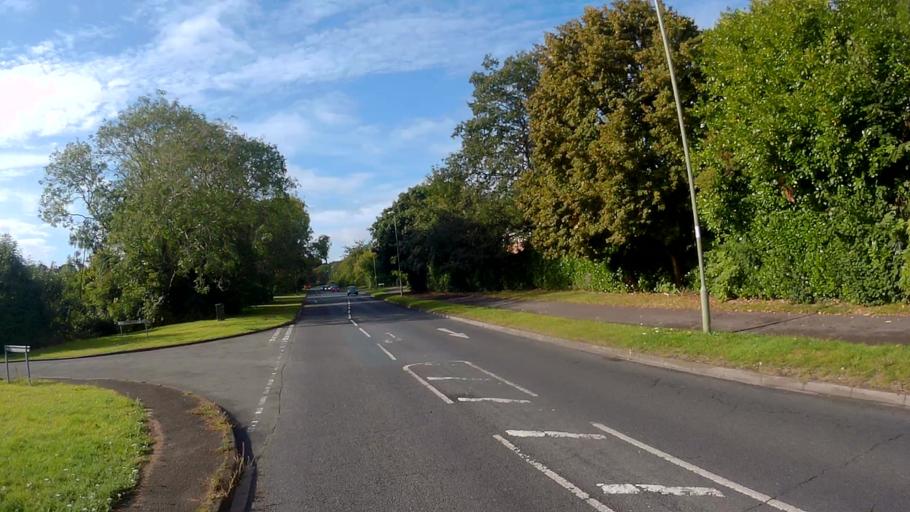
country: GB
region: England
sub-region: Hampshire
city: Basingstoke
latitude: 51.2451
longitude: -1.1024
